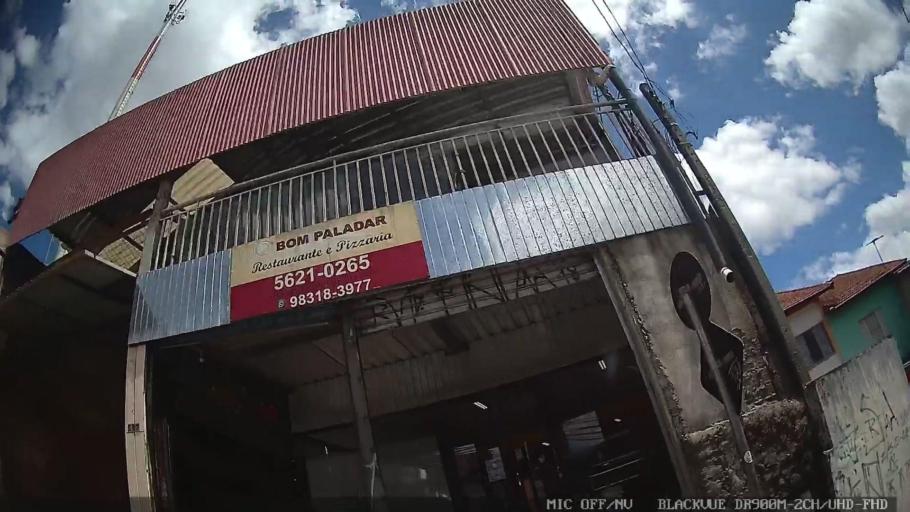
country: BR
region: Sao Paulo
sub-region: Diadema
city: Diadema
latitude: -23.6699
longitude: -46.6411
